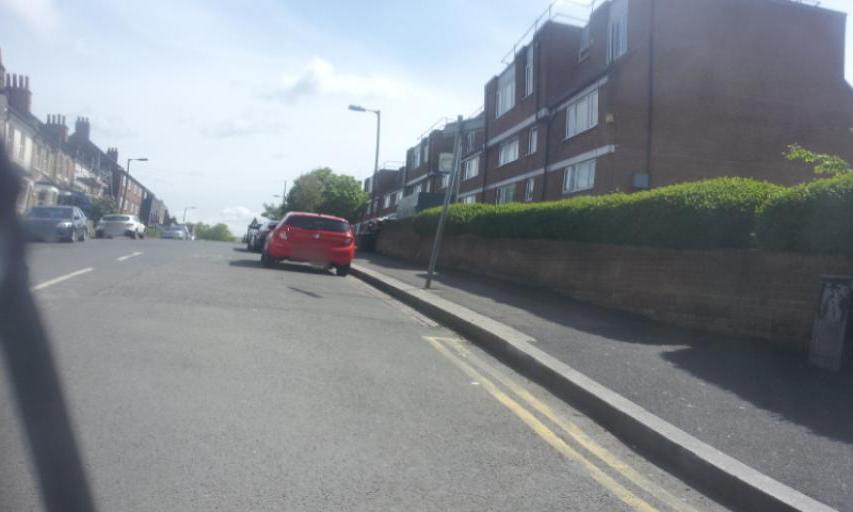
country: GB
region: England
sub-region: Greater London
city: Catford
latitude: 51.4583
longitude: -0.0541
